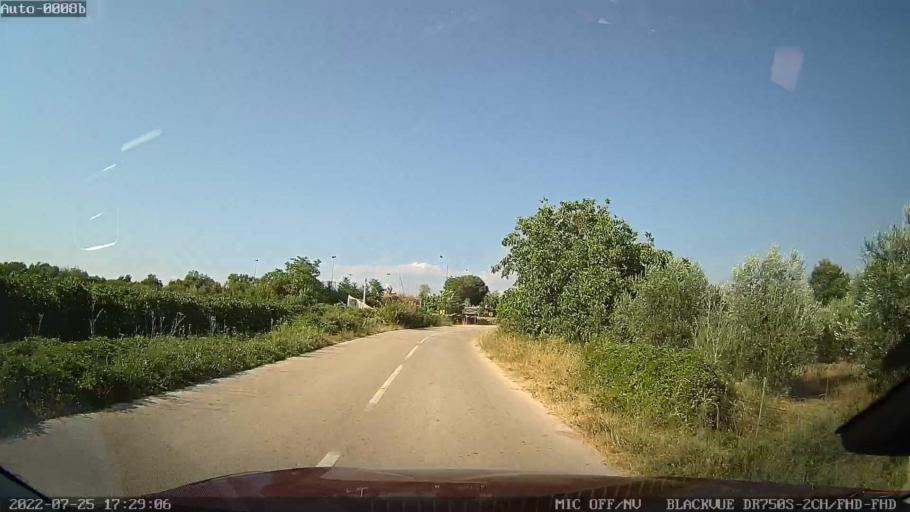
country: HR
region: Zadarska
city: Pridraga
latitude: 44.1587
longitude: 15.5116
